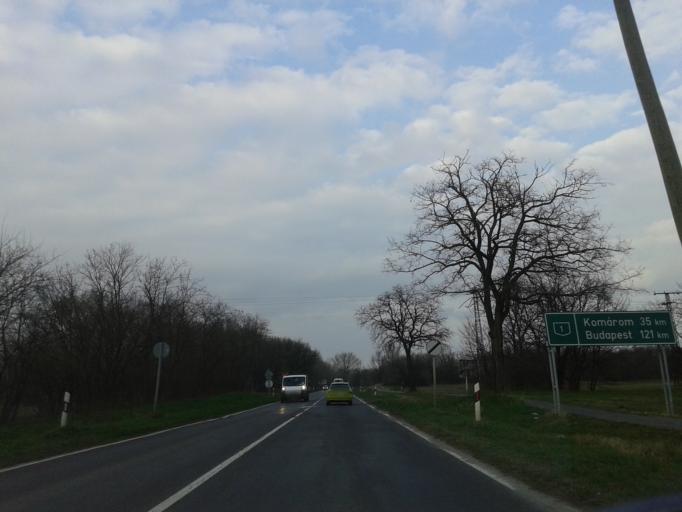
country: HU
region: Gyor-Moson-Sopron
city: Gyor
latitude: 47.7142
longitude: 17.6796
